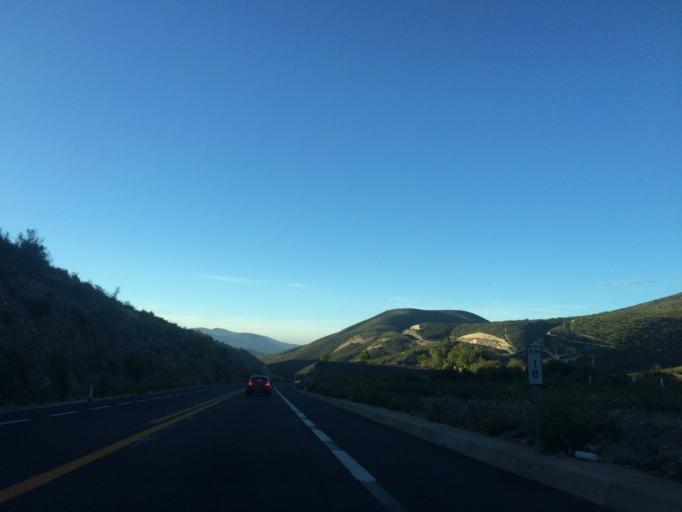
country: MX
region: Puebla
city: Chapuco
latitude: 18.6699
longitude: -97.4578
